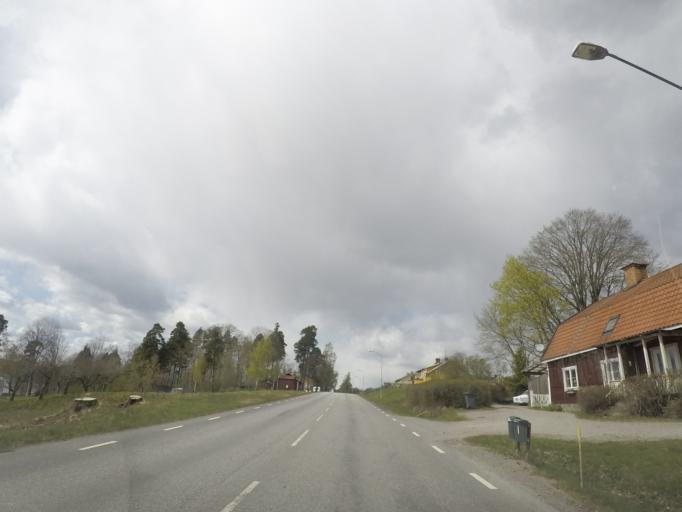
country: SE
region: Soedermanland
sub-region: Katrineholms Kommun
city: Katrineholm
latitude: 58.9531
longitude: 16.2939
